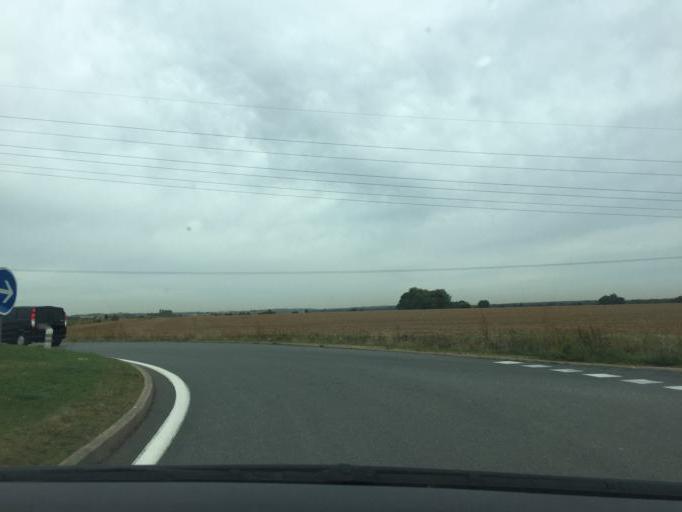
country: FR
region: Ile-de-France
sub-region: Departement de l'Essonne
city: Villiers-le-Bacle
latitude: 48.7294
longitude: 2.1279
